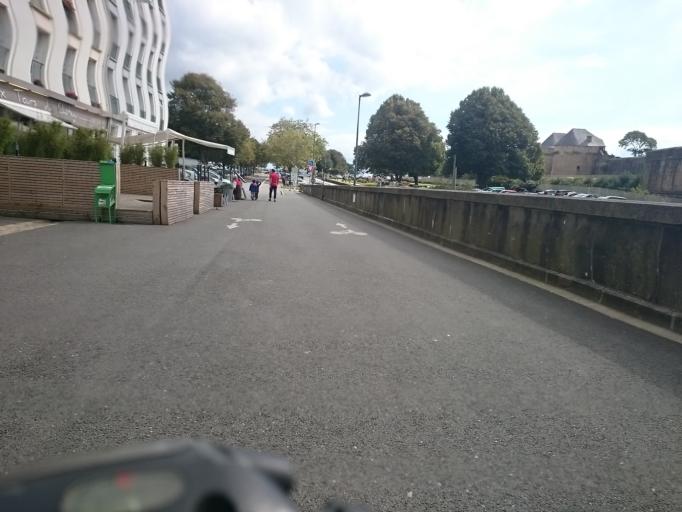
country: FR
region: Brittany
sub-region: Departement du Finistere
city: Brest
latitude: 48.3839
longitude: -4.4941
